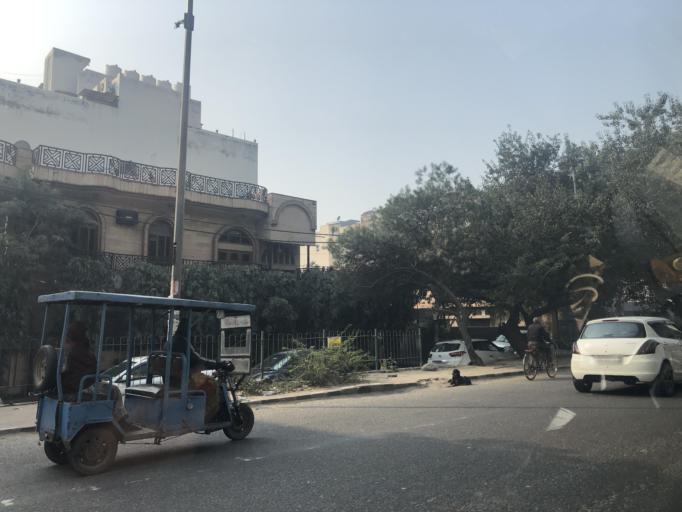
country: IN
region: NCT
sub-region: North West Delhi
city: Pitampura
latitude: 28.6779
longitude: 77.1066
